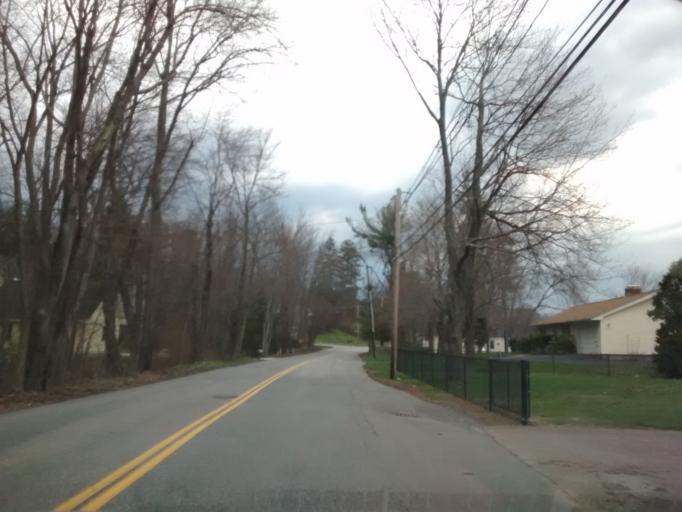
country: US
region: Massachusetts
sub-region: Worcester County
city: Sutton
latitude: 42.1679
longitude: -71.7873
